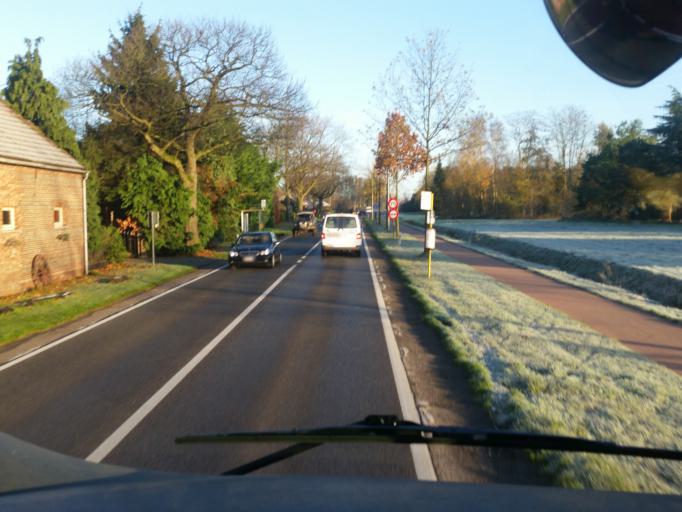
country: BE
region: Flanders
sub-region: Provincie Antwerpen
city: Arendonk
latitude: 51.2979
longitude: 5.0934
